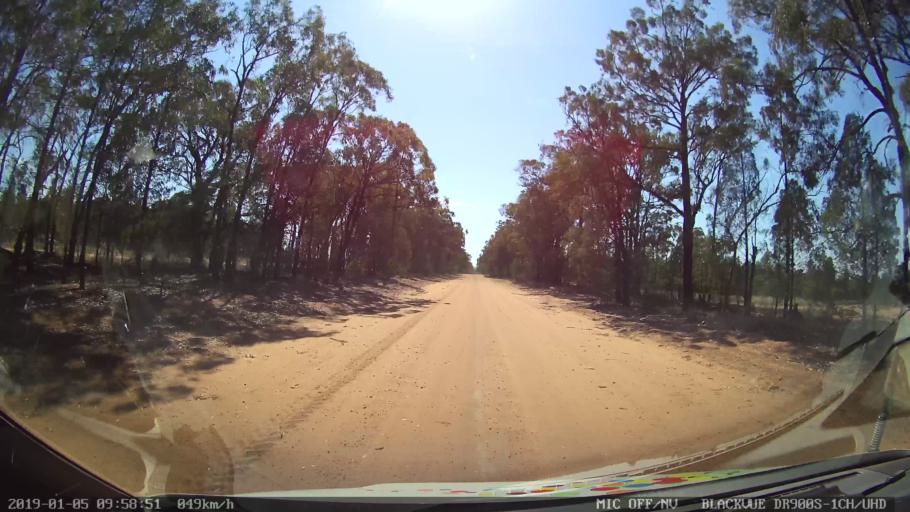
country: AU
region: New South Wales
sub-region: Gilgandra
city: Gilgandra
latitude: -31.6670
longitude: 148.8131
